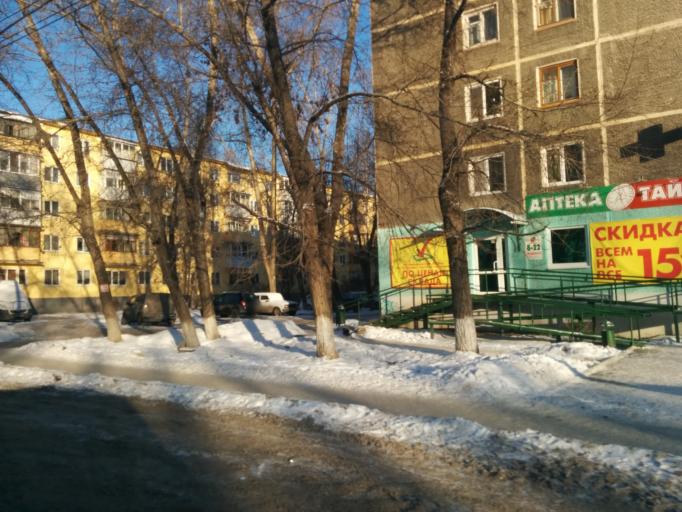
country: RU
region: Perm
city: Overyata
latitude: 58.0077
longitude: 55.9331
